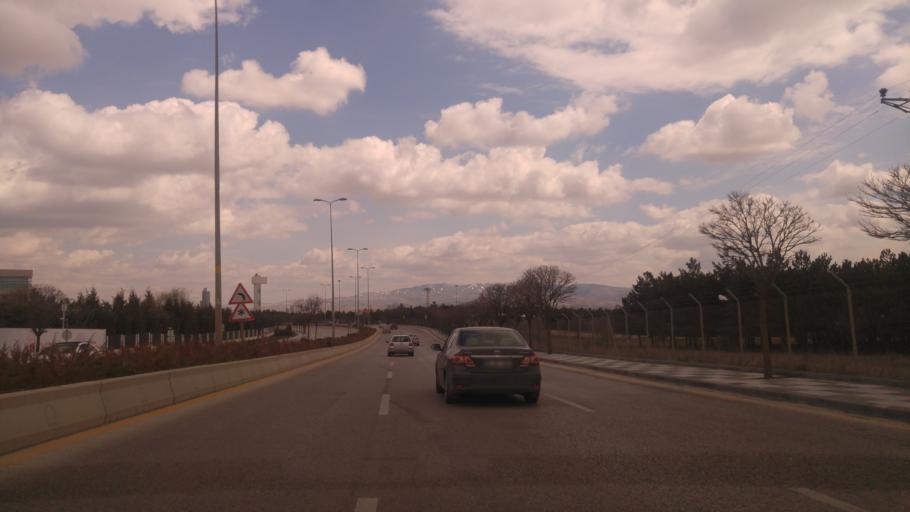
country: TR
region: Ankara
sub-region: Goelbasi
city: Golbasi
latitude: 39.8439
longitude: 32.7858
